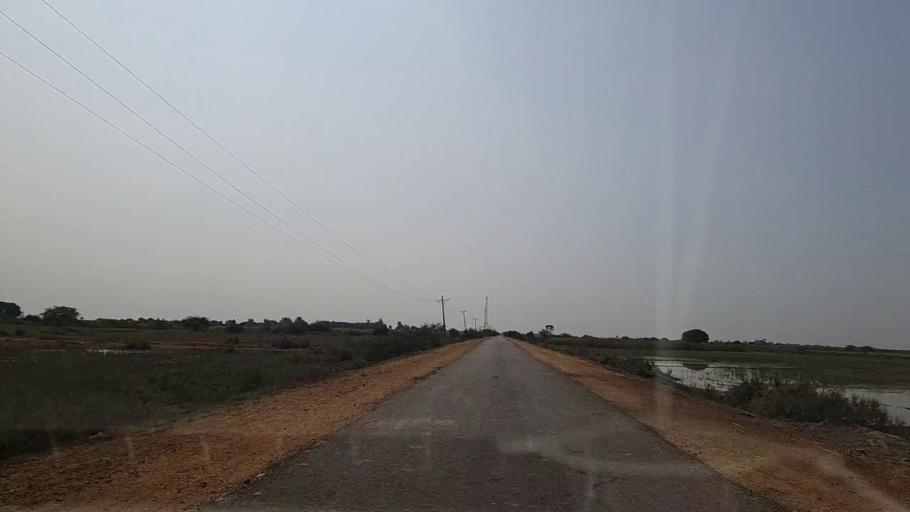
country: PK
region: Sindh
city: Chuhar Jamali
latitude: 24.2915
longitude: 67.9265
